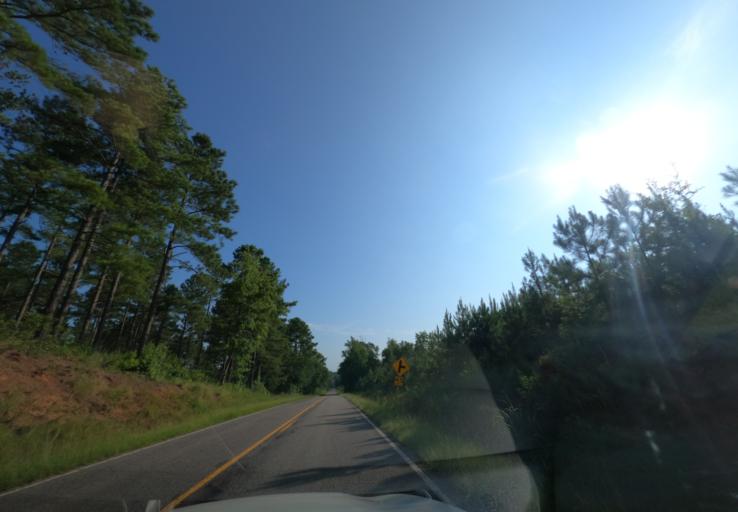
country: US
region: South Carolina
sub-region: Edgefield County
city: Edgefield
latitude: 33.7455
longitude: -81.9605
